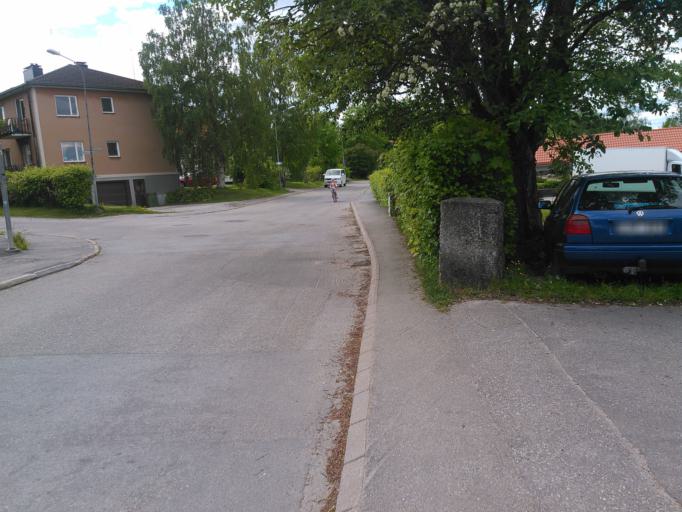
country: SE
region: Vaesterbotten
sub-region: Umea Kommun
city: Umea
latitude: 63.8232
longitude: 20.2463
